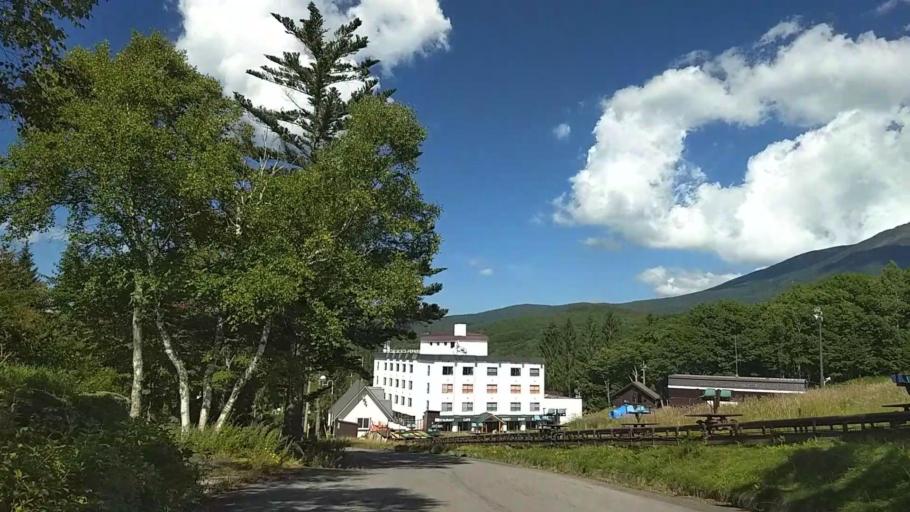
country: JP
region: Nagano
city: Chino
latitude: 36.1014
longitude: 138.2334
